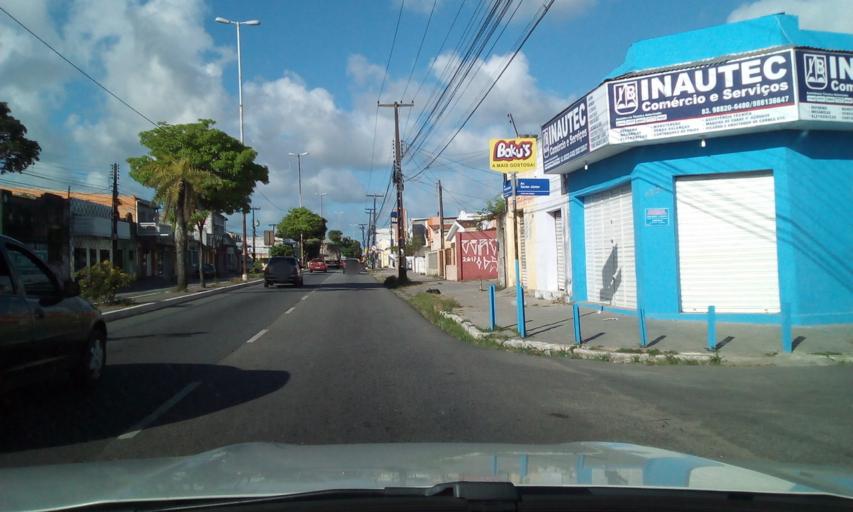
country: BR
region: Paraiba
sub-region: Joao Pessoa
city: Joao Pessoa
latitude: -7.1420
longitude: -34.8900
